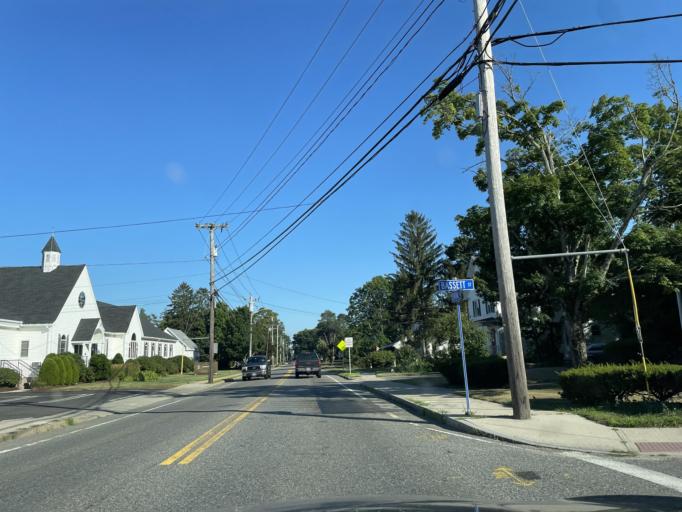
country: US
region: Massachusetts
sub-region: Norfolk County
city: Foxborough
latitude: 42.0604
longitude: -71.2463
